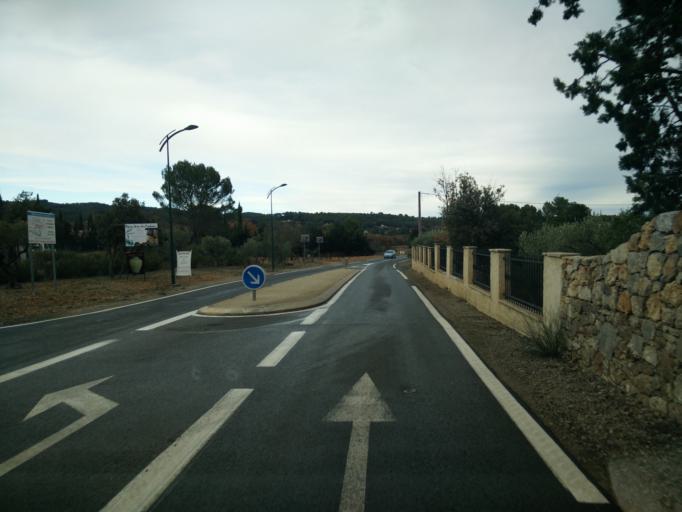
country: FR
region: Provence-Alpes-Cote d'Azur
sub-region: Departement du Var
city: Cotignac
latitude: 43.5101
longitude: 6.1563
